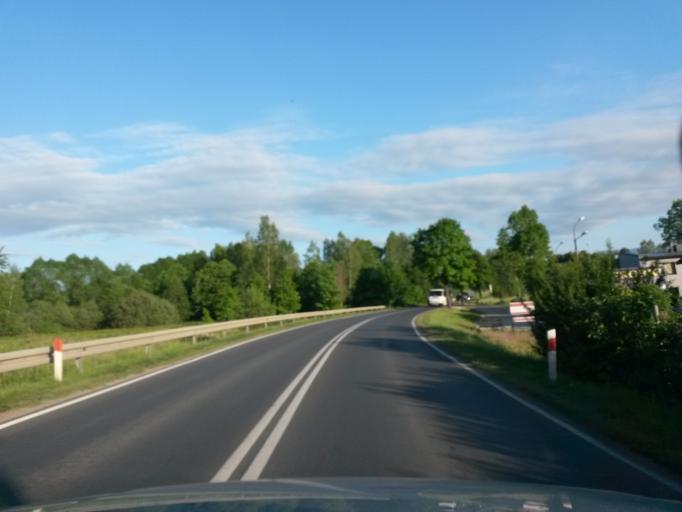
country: PL
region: Lower Silesian Voivodeship
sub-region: Jelenia Gora
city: Jelenia Gora
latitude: 50.8846
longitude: 15.7576
